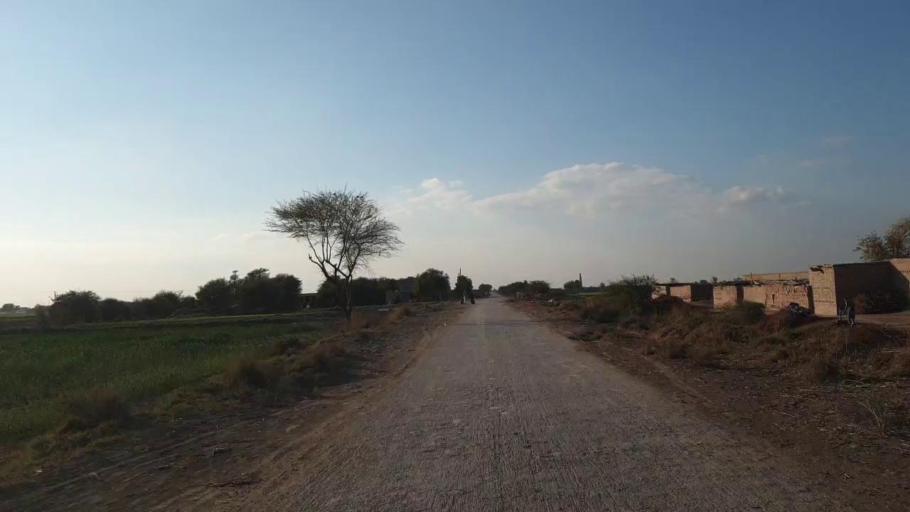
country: PK
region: Sindh
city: Shahpur Chakar
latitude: 26.1437
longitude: 68.5414
